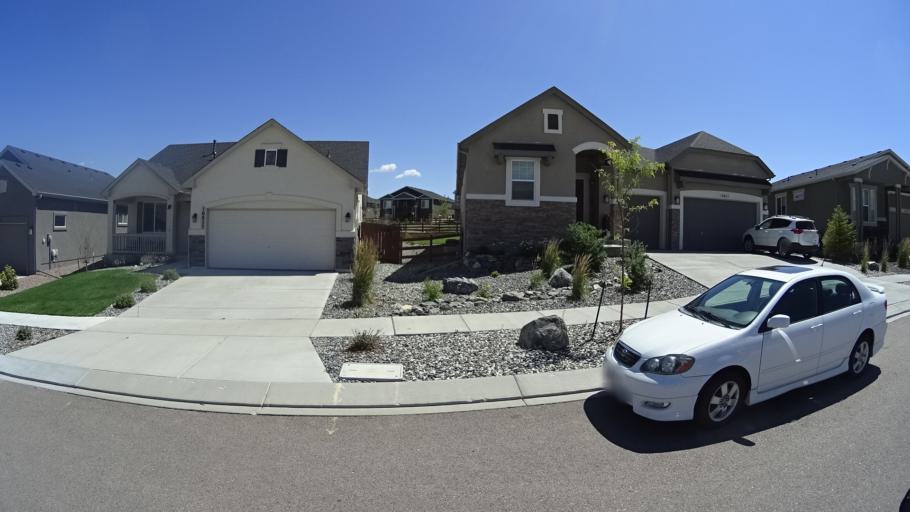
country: US
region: Colorado
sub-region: El Paso County
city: Black Forest
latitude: 38.9906
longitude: -104.7635
